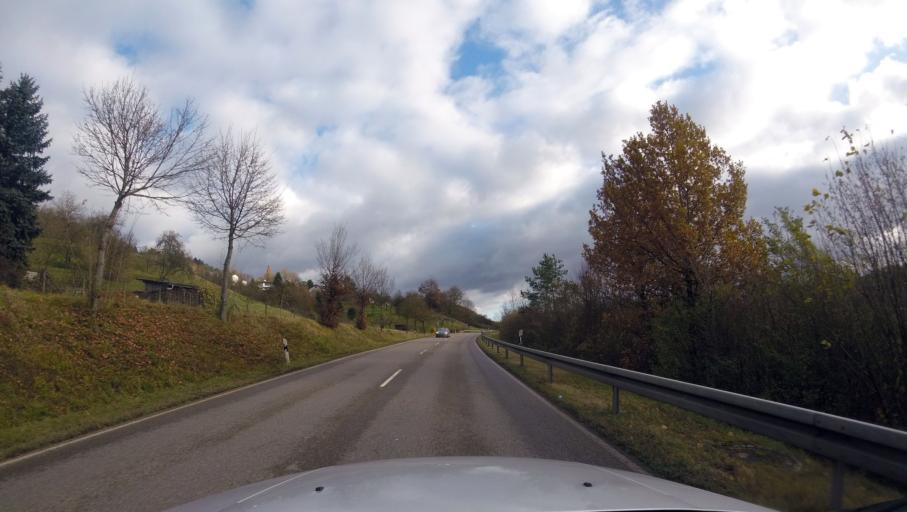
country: DE
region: Baden-Wuerttemberg
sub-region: Regierungsbezirk Stuttgart
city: Murrhardt
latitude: 48.9849
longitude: 9.5667
